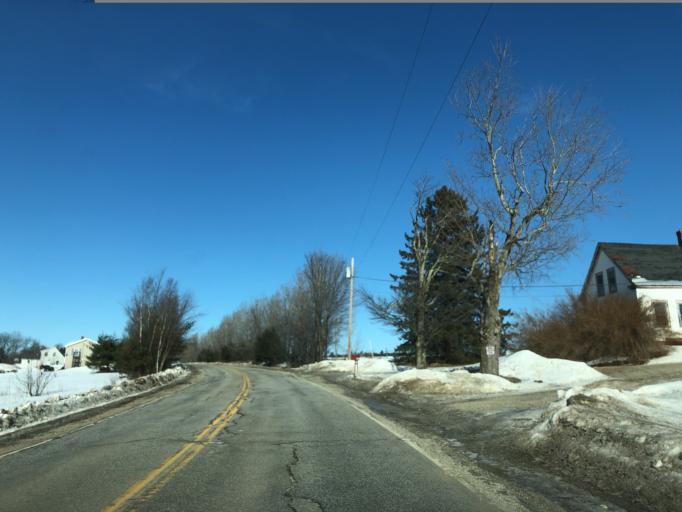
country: US
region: Maine
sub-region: Oxford County
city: Buckfield
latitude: 44.2342
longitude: -70.3349
